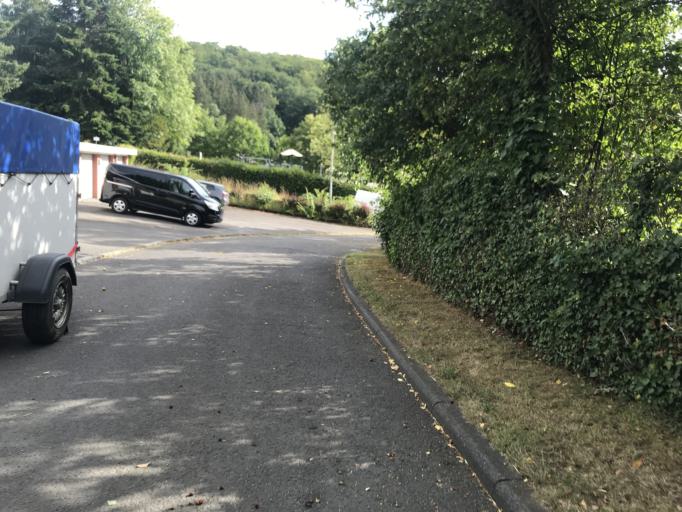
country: DE
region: Hesse
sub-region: Regierungsbezirk Giessen
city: Lohra
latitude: 50.6682
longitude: 8.6045
